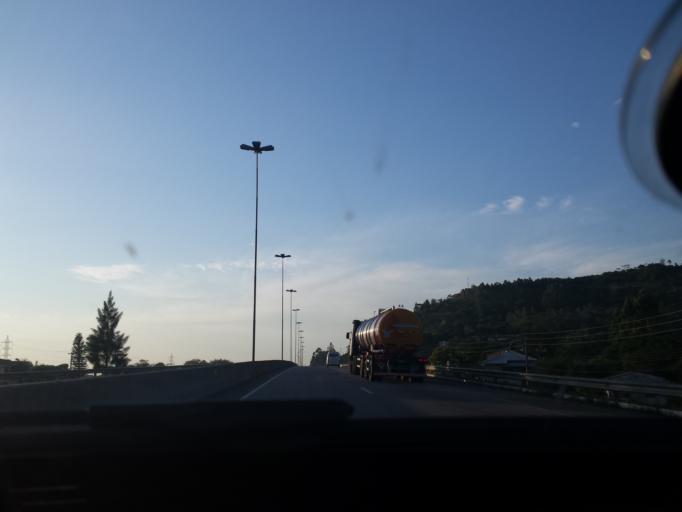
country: BR
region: Santa Catarina
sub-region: Imbituba
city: Imbituba
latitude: -28.0640
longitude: -48.7159
